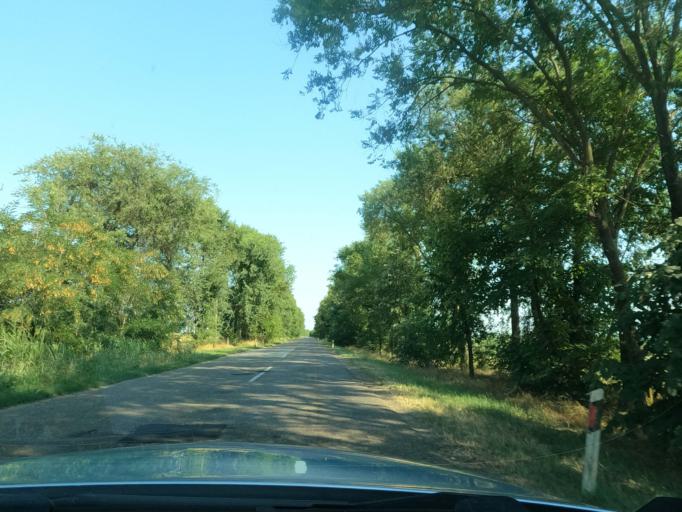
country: RS
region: Autonomna Pokrajina Vojvodina
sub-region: Juznobacki Okrug
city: Becej
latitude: 45.6654
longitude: 19.9389
